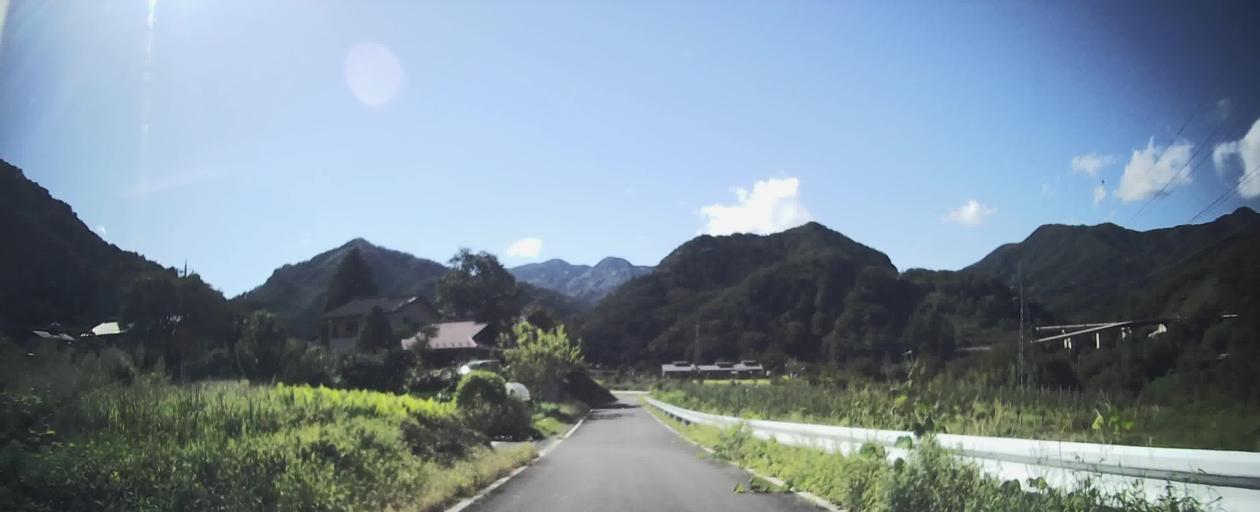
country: JP
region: Gunma
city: Nakanojomachi
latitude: 36.5691
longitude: 138.7397
